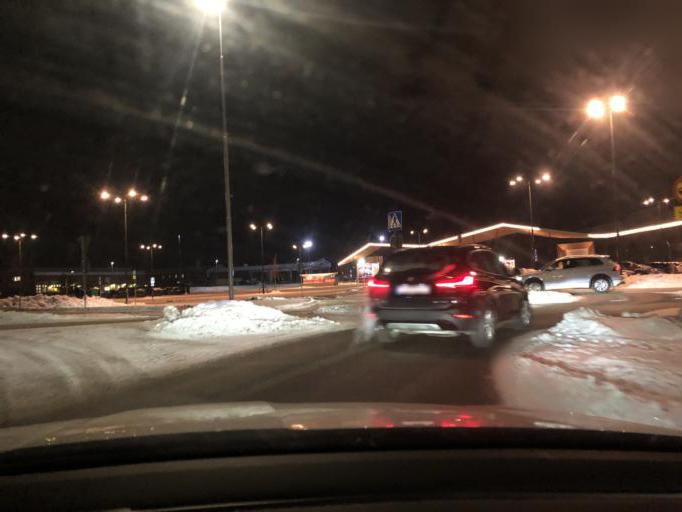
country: SE
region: Uppsala
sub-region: Uppsala Kommun
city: Saevja
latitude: 59.8437
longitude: 17.7112
